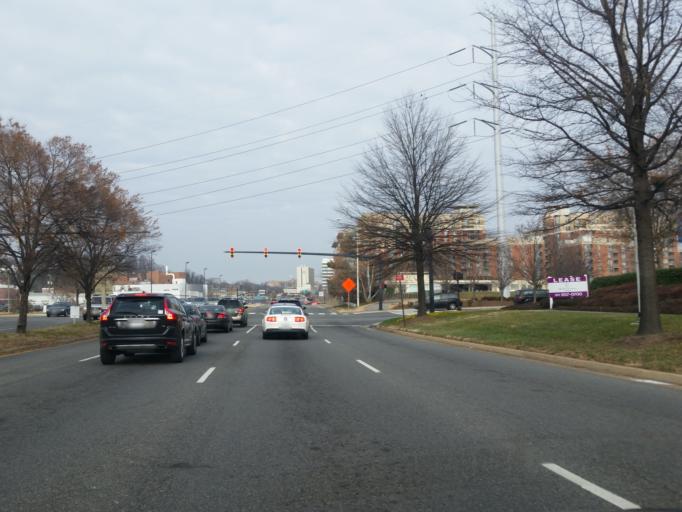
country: US
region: Virginia
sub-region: City of Alexandria
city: Alexandria
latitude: 38.8393
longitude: -77.0521
